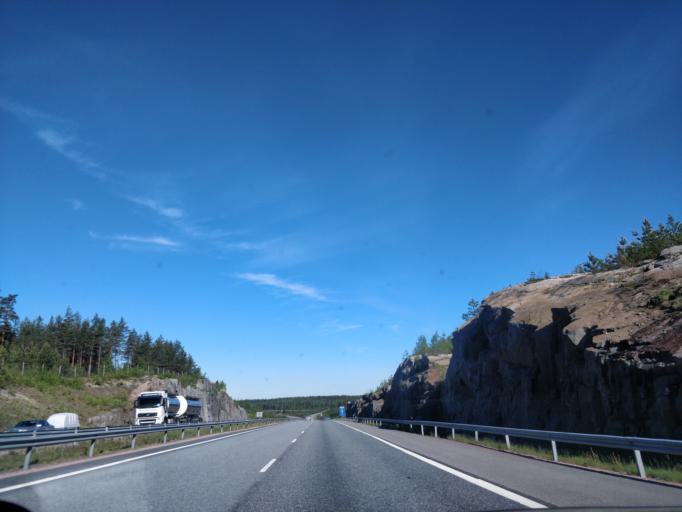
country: FI
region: Varsinais-Suomi
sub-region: Salo
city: Suomusjaervi
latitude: 60.3757
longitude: 23.6391
